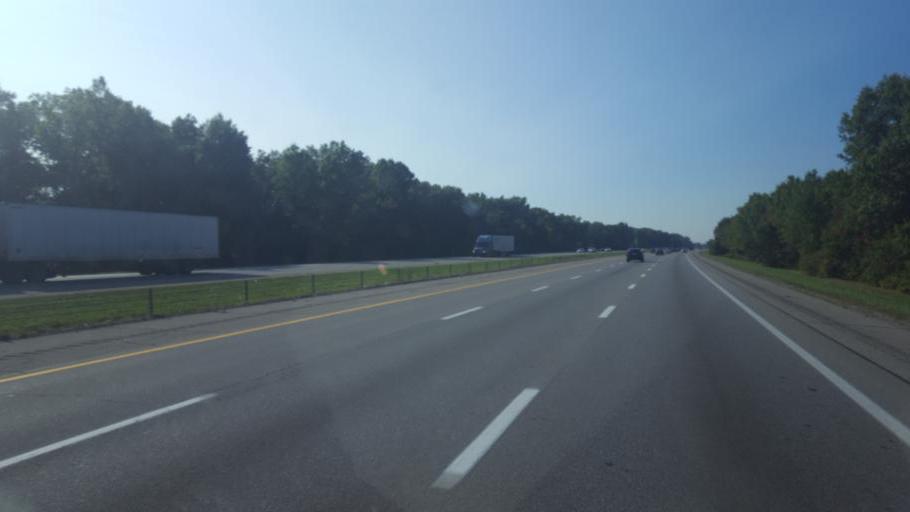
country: US
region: Ohio
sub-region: Delaware County
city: Sunbury
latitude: 40.2381
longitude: -82.9286
